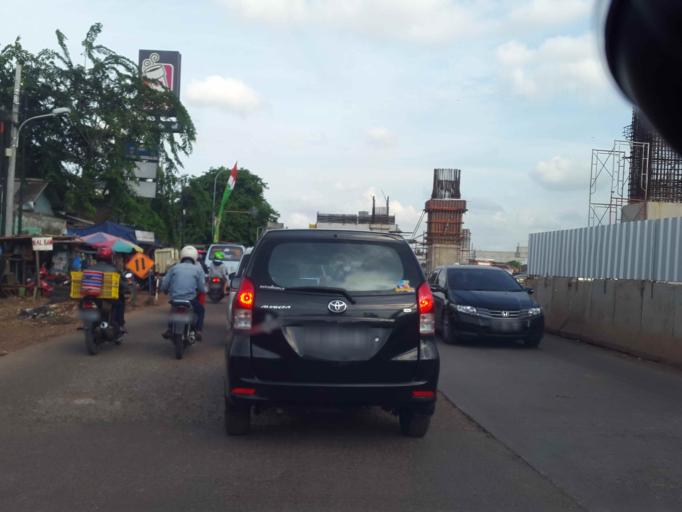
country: ID
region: West Java
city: Bekasi
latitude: -6.2495
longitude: 106.9429
